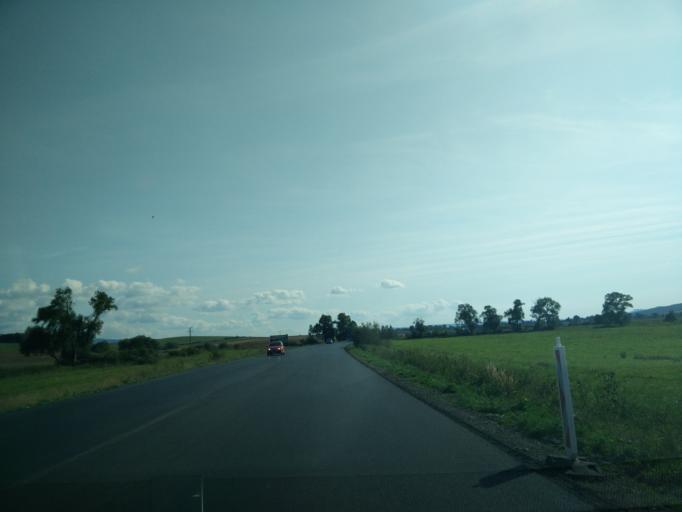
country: SK
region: Zilinsky
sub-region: Okres Martin
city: Martin
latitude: 49.0147
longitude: 18.8994
